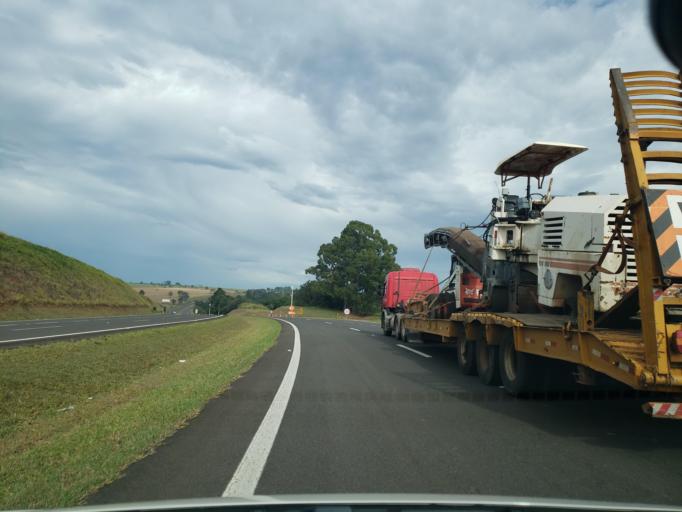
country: BR
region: Sao Paulo
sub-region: Dois Corregos
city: Dois Corregos
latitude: -22.2501
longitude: -48.3596
